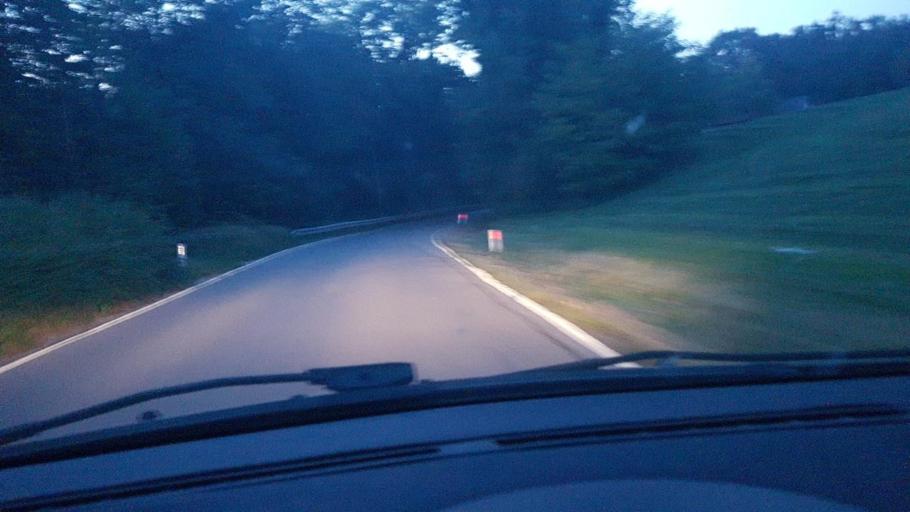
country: SI
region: Maribor
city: Kamnica
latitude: 46.5708
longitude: 15.6262
